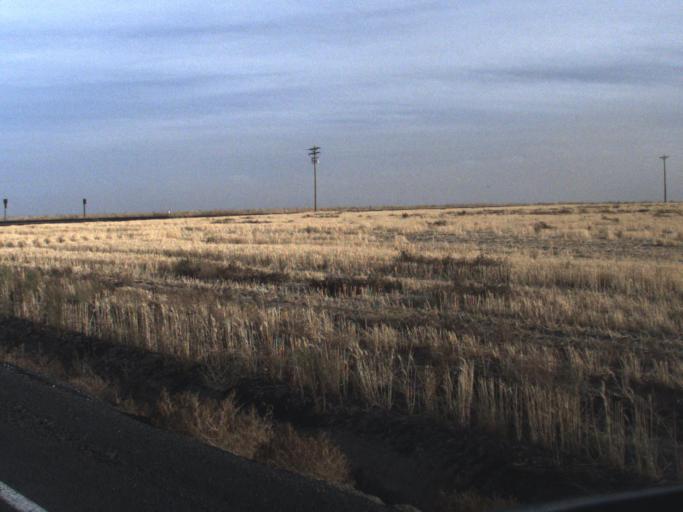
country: US
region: Washington
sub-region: Adams County
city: Ritzville
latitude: 47.2611
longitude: -118.6874
